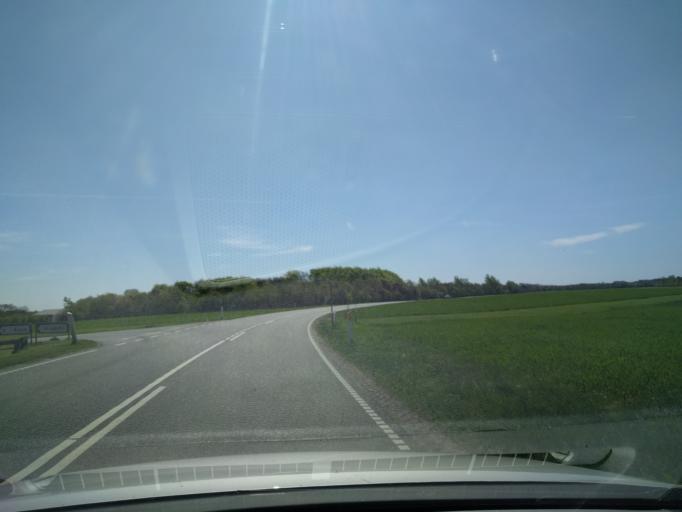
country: DK
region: Central Jutland
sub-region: Ringkobing-Skjern Kommune
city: Tarm
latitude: 55.8849
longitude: 8.5246
